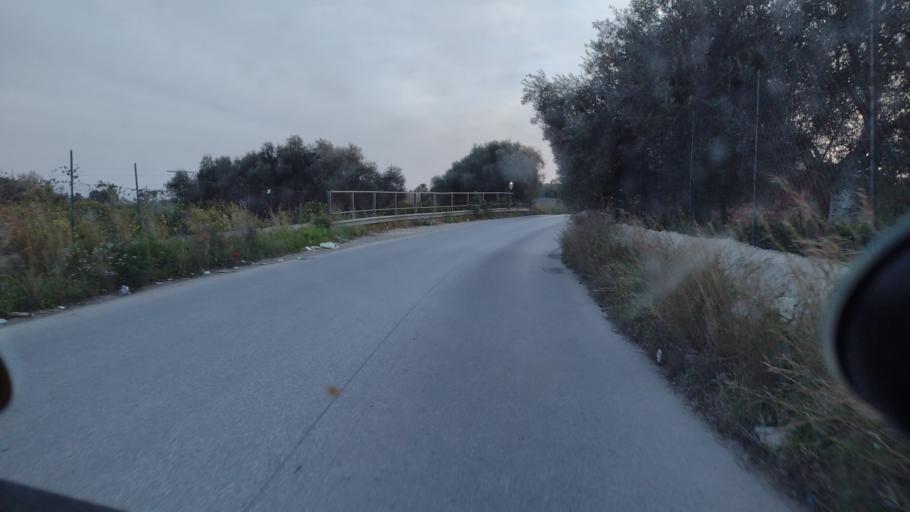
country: IT
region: Sicily
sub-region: Provincia di Siracusa
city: Avola
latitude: 36.8909
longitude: 15.1327
